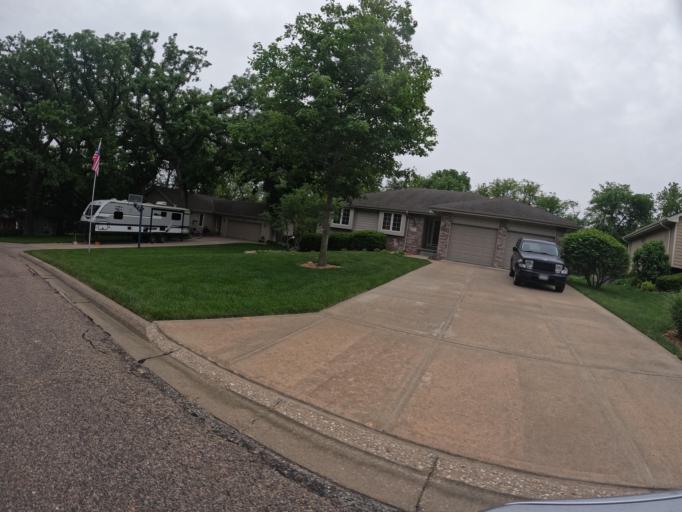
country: US
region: Nebraska
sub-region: Sarpy County
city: Offutt Air Force Base
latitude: 41.0448
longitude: -95.9726
